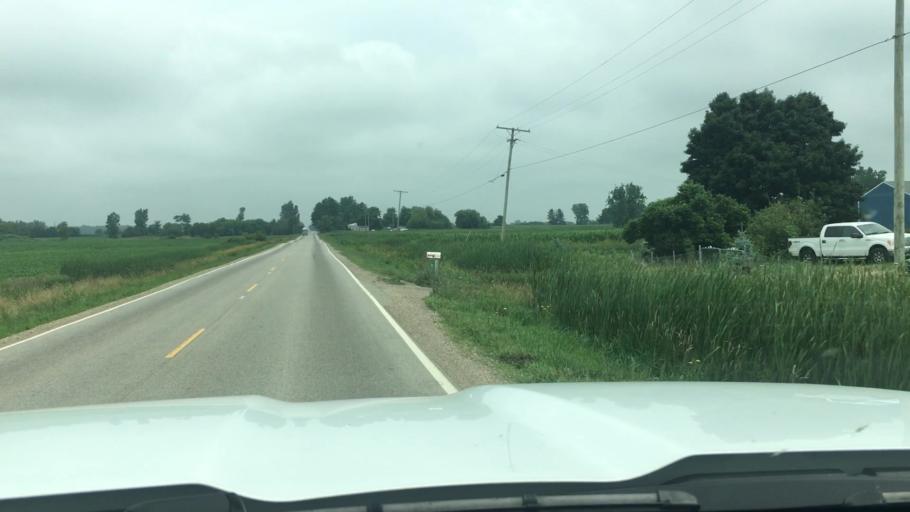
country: US
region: Michigan
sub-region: Sanilac County
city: Brown City
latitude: 43.2604
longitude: -82.9820
